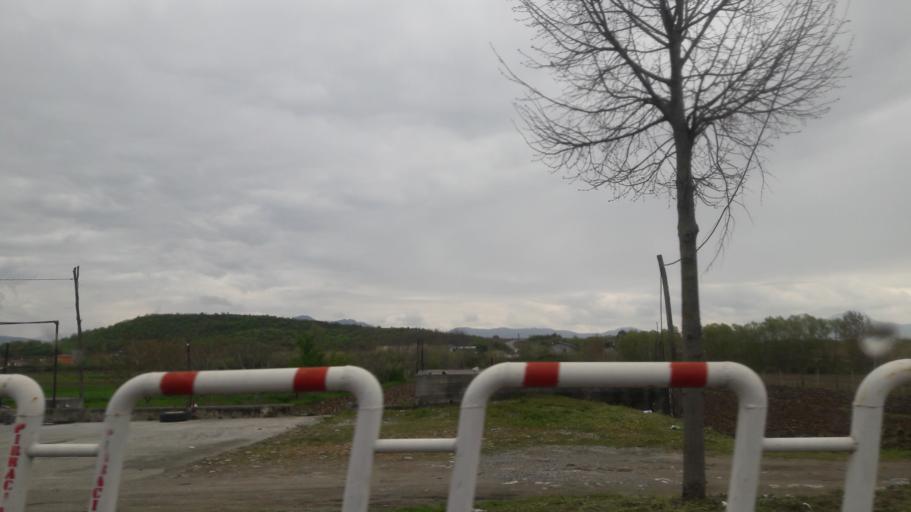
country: AL
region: Shkoder
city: Vukatane
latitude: 41.9617
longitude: 19.5368
